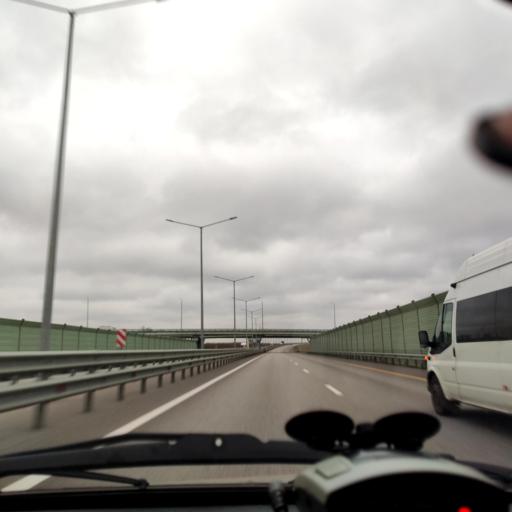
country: RU
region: Voronezj
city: Novaya Usman'
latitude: 51.6035
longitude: 39.3360
